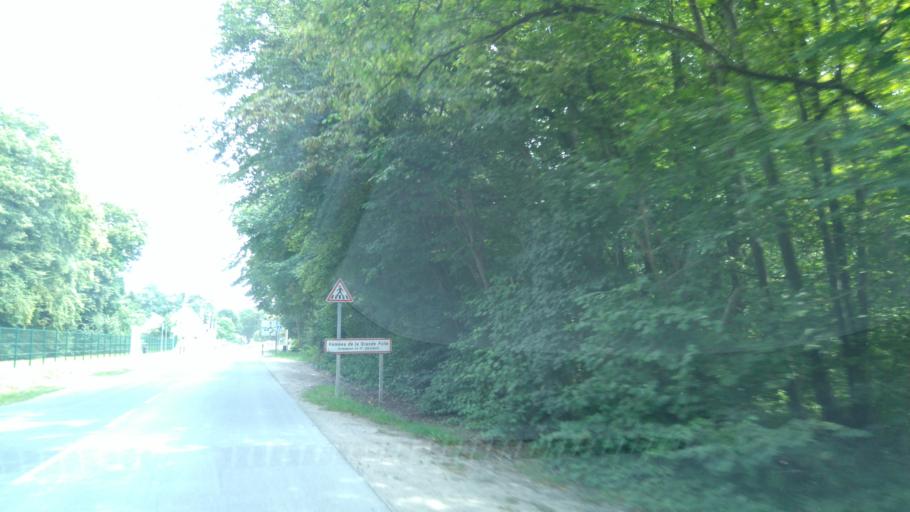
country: FR
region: Picardie
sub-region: Departement de l'Oise
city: Saint-Maximin
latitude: 49.2216
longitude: 2.4638
